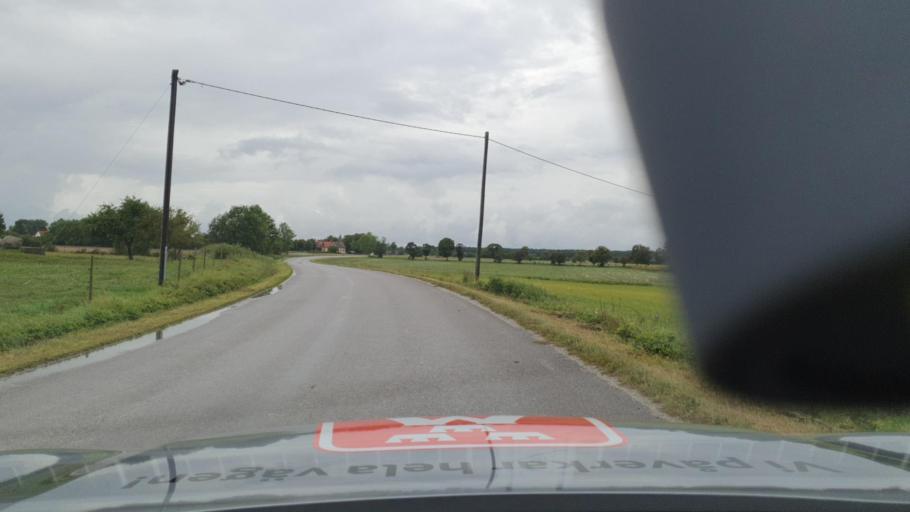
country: SE
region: Gotland
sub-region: Gotland
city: Visby
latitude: 57.5620
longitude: 18.5617
